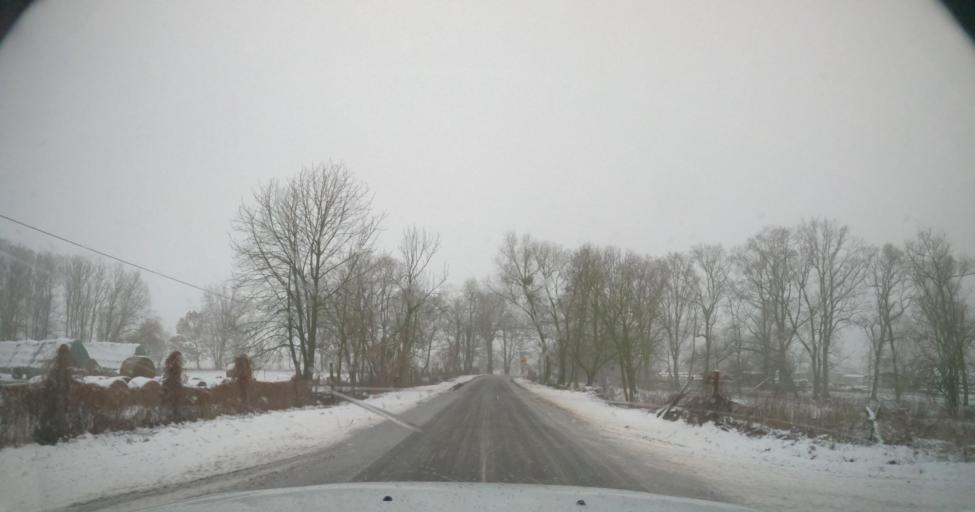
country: PL
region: West Pomeranian Voivodeship
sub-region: Powiat goleniowski
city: Stepnica
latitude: 53.5657
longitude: 14.6816
